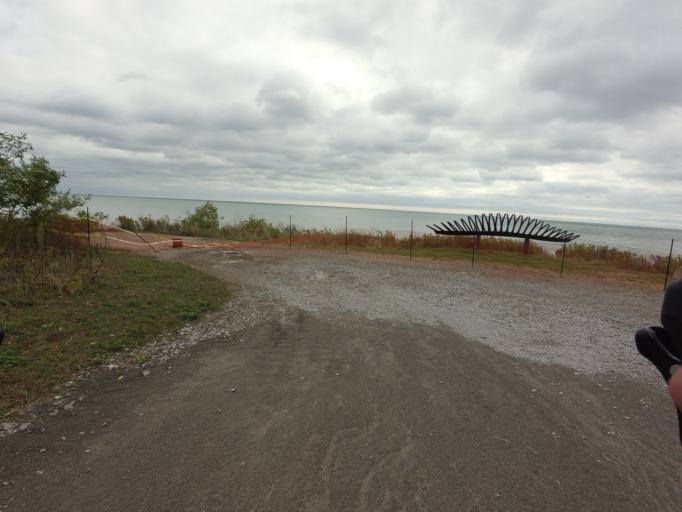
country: CA
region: Ontario
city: Scarborough
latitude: 43.7272
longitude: -79.2138
